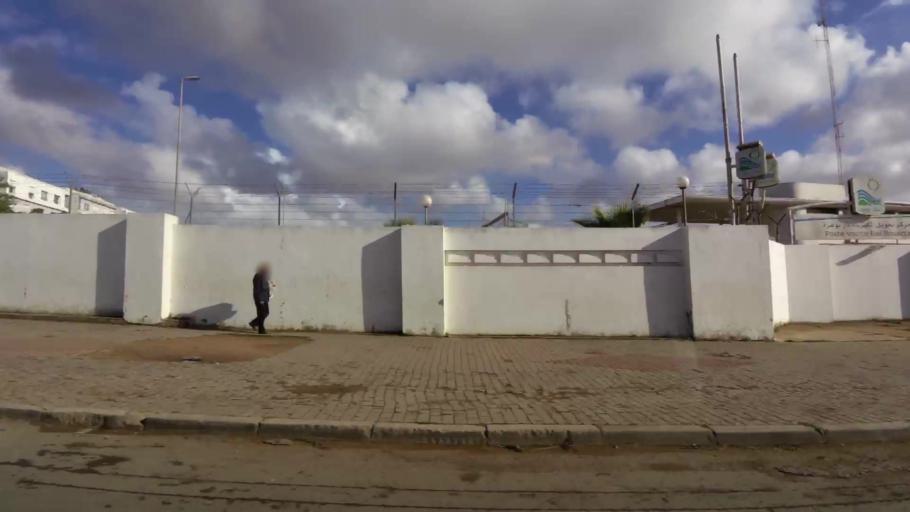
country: MA
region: Grand Casablanca
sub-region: Casablanca
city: Casablanca
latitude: 33.5510
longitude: -7.6958
